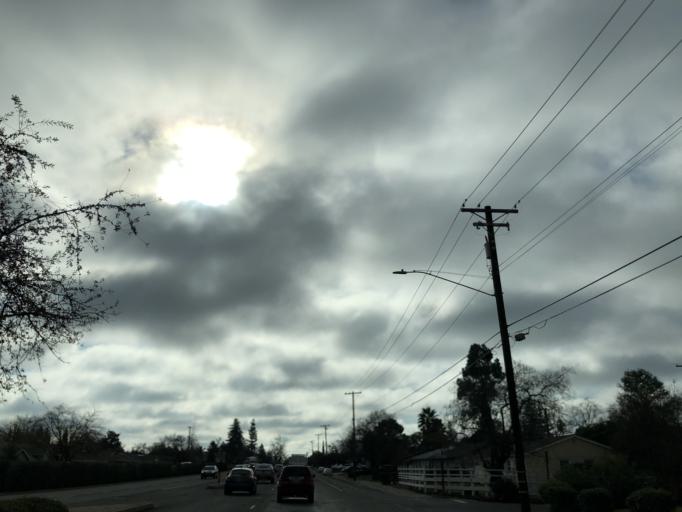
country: US
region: California
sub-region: Sacramento County
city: Arden-Arcade
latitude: 38.5921
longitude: -121.3832
